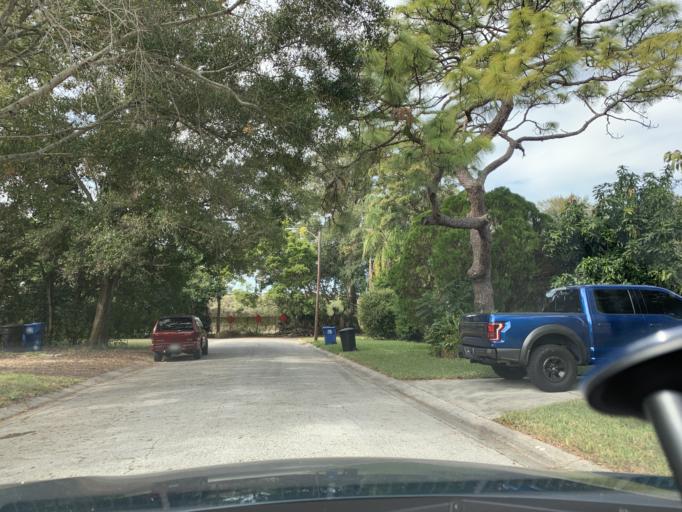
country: US
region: Florida
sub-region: Pinellas County
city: Saint Petersburg
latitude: 27.7929
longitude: -82.6593
